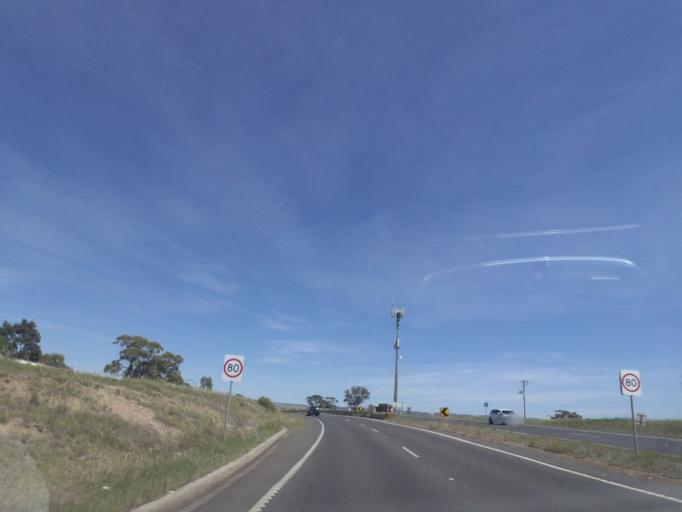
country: AU
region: Victoria
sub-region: Melton
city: Brookfield
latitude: -37.6804
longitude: 144.5047
